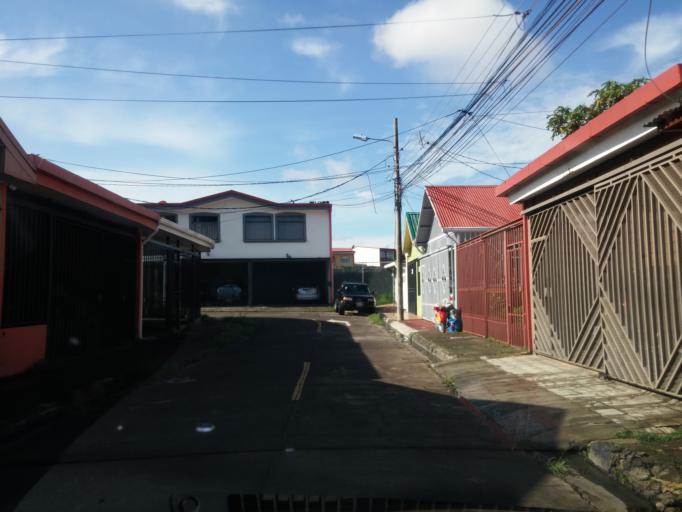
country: CR
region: Heredia
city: Mercedes
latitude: 10.0054
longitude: -84.1438
